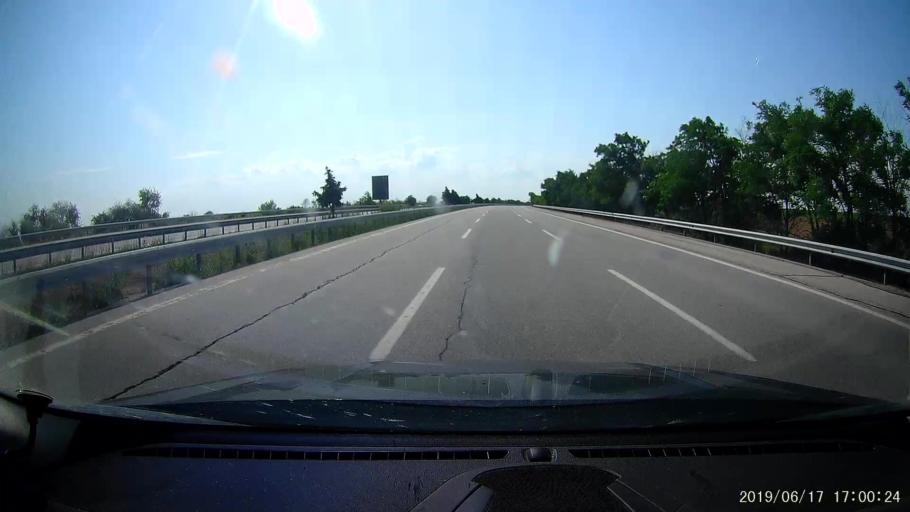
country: TR
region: Edirne
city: Haskoy
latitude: 41.6202
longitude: 26.8328
